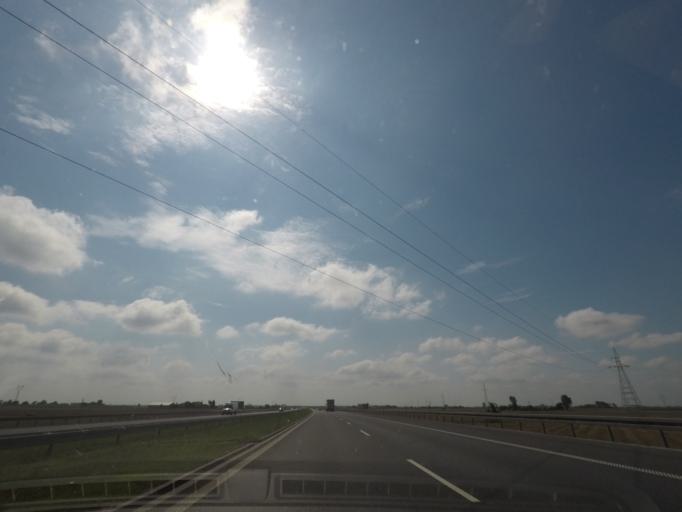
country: PL
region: Kujawsko-Pomorskie
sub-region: Powiat wloclawski
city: Lubanie
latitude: 52.7276
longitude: 18.8625
